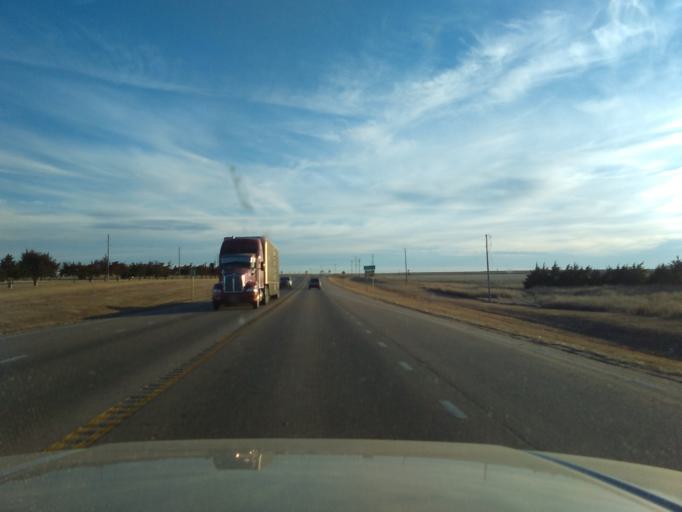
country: US
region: Kansas
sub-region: Logan County
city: Oakley
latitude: 39.1228
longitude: -100.8683
